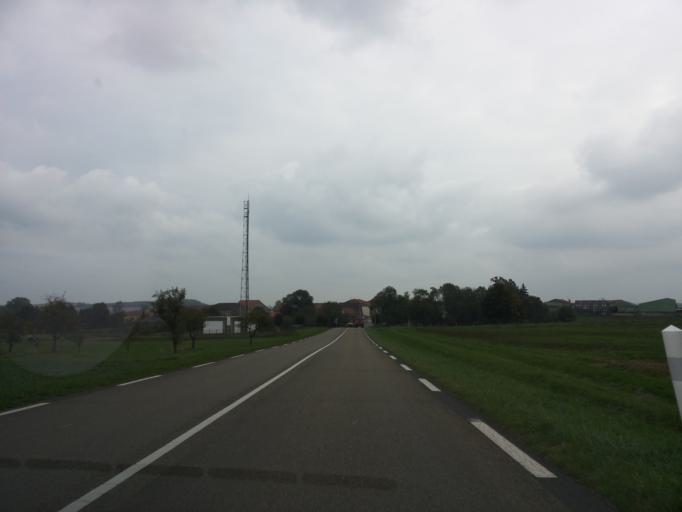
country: FR
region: Lorraine
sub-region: Departement de la Moselle
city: Vic-sur-Seille
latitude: 48.7536
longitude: 6.6220
